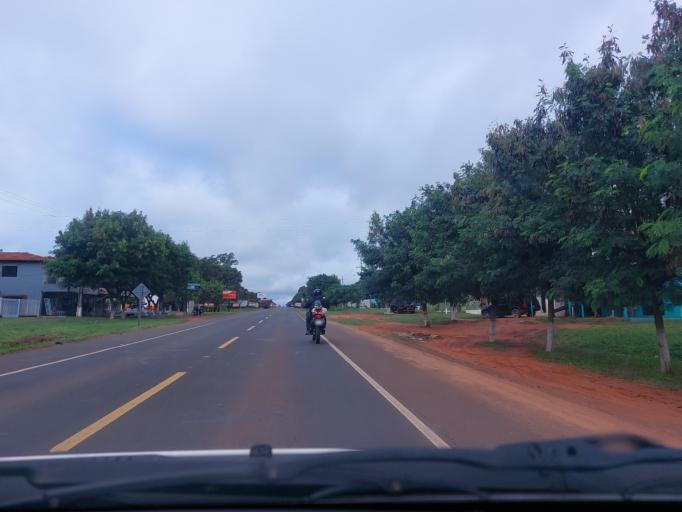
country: PY
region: San Pedro
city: Guayaybi
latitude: -24.5678
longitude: -56.4030
